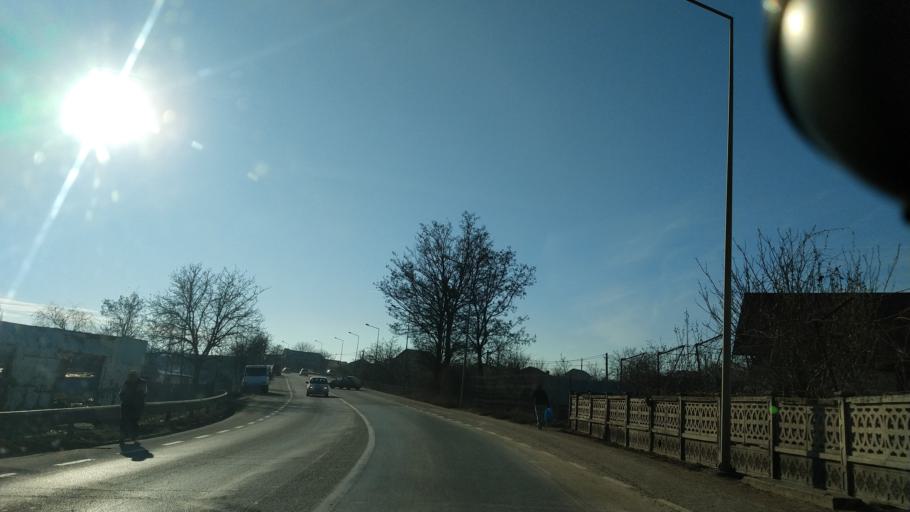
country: RO
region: Iasi
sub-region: Comuna Targu Frumos
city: Targu Frumos
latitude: 47.2023
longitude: 27.0004
